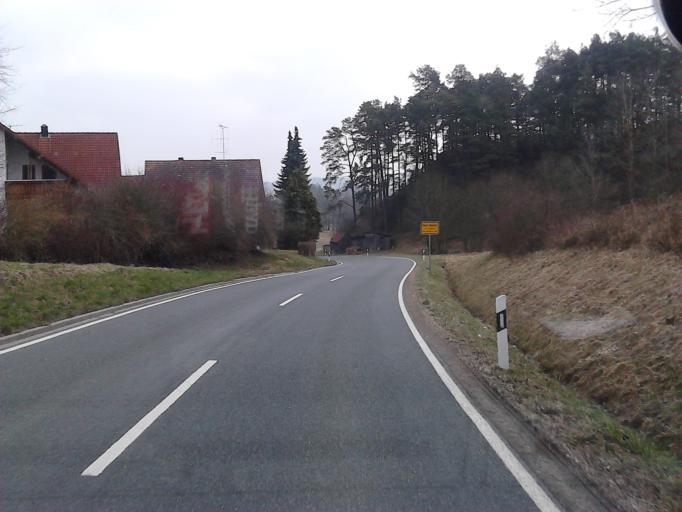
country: DE
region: Bavaria
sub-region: Regierungsbezirk Mittelfranken
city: Neuhaus an der Pegnitz
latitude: 49.6335
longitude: 11.5440
